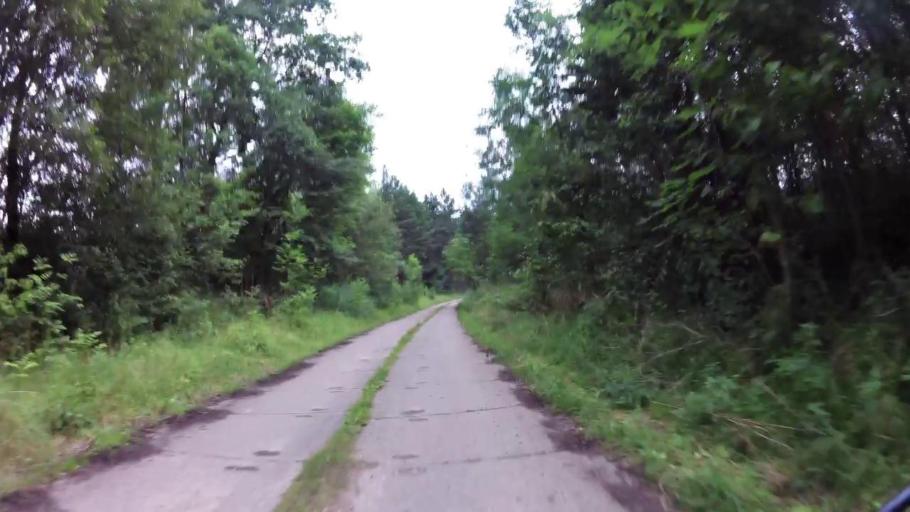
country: PL
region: West Pomeranian Voivodeship
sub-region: Powiat drawski
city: Drawsko Pomorskie
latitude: 53.5644
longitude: 15.8521
